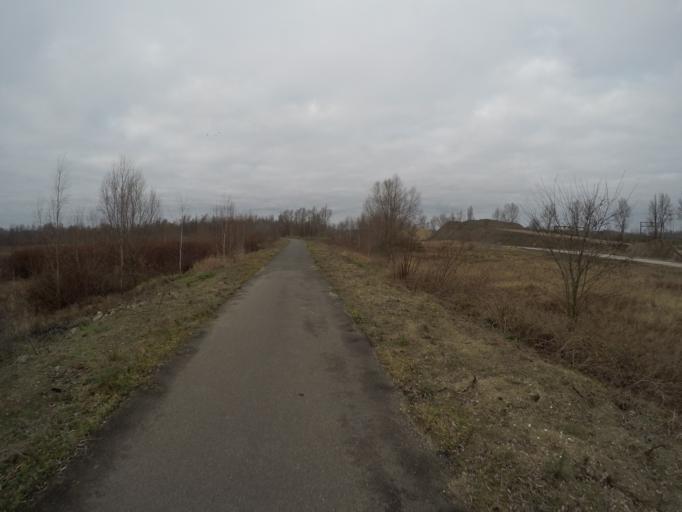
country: BE
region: Flanders
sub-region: Provincie Antwerpen
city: Zwijndrecht
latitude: 51.2116
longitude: 4.3612
